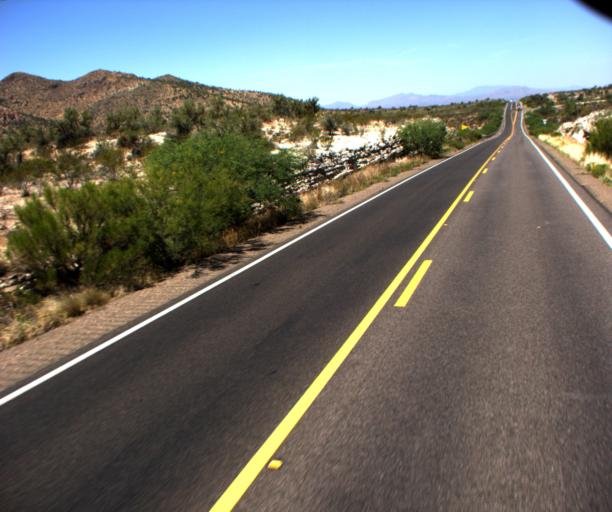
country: US
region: Arizona
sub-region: Gila County
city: Peridot
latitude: 33.2861
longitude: -110.3660
